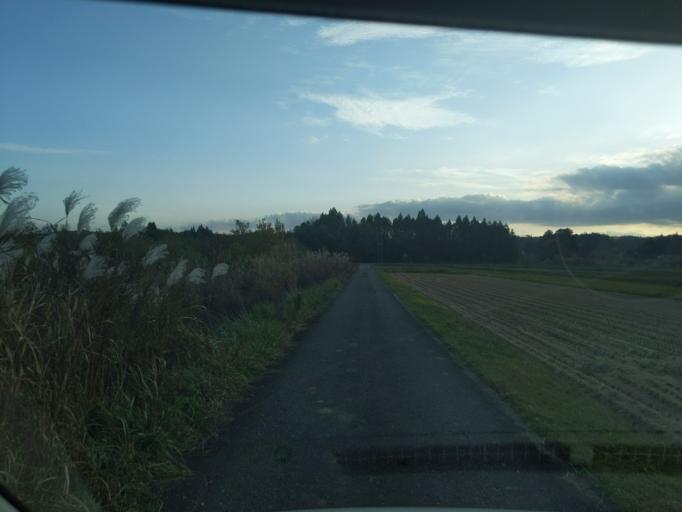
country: JP
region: Iwate
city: Ichinoseki
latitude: 38.9504
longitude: 141.0447
